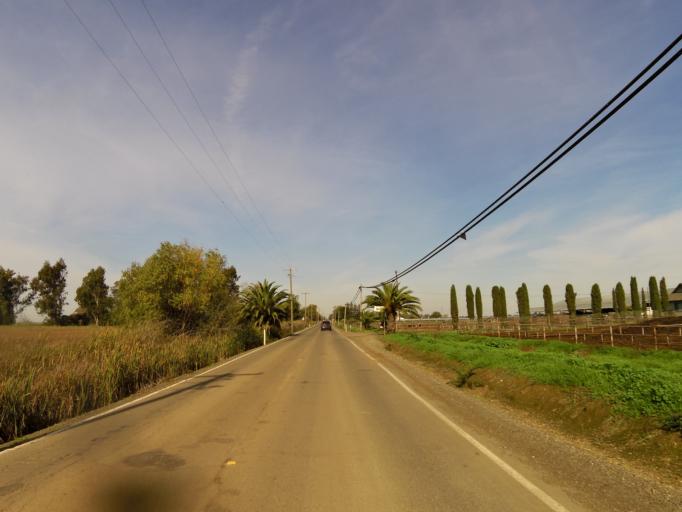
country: US
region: California
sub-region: Sacramento County
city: Laguna
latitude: 38.3431
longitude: -121.4174
